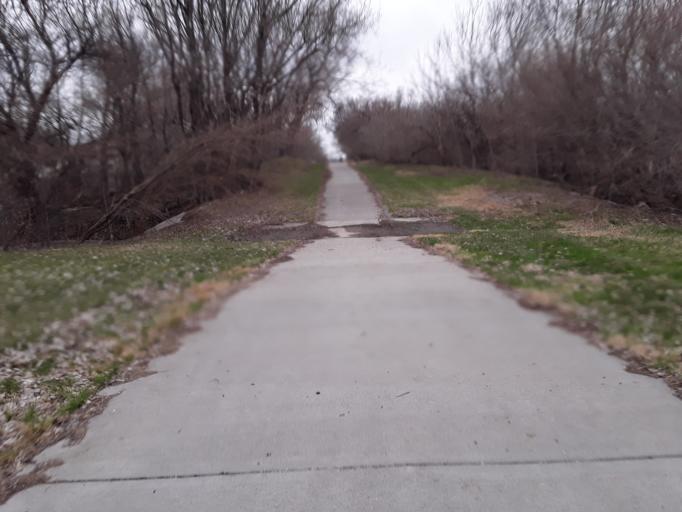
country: US
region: Nebraska
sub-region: Lancaster County
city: Lincoln
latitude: 40.8513
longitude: -96.6185
